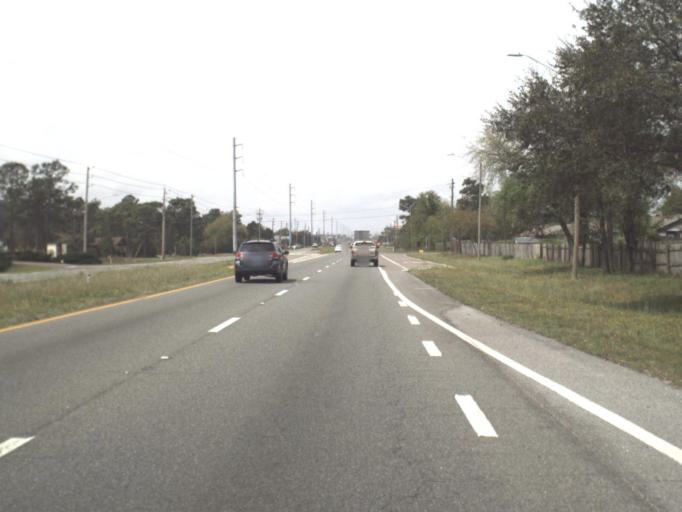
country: US
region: Florida
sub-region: Santa Rosa County
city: Tiger Point
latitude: 30.3889
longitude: -87.0738
